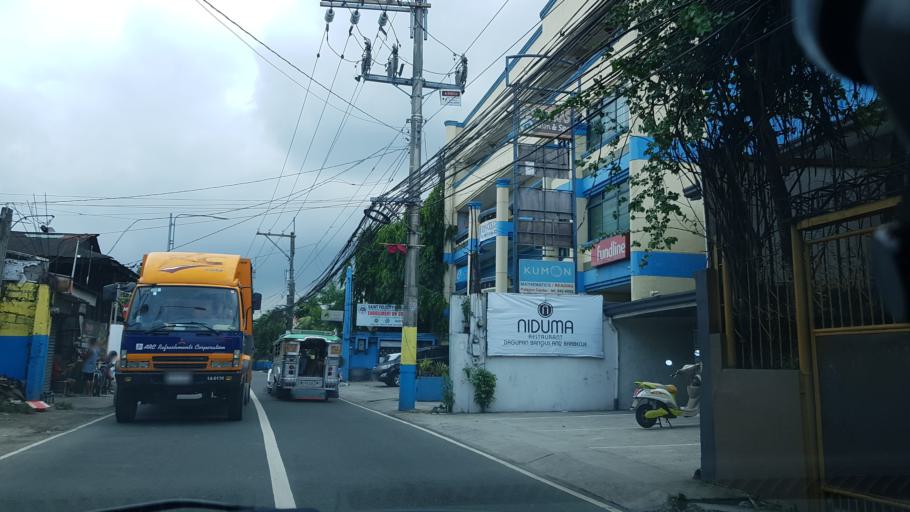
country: PH
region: Calabarzon
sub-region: Province of Rizal
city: Pateros
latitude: 14.5470
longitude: 121.0704
